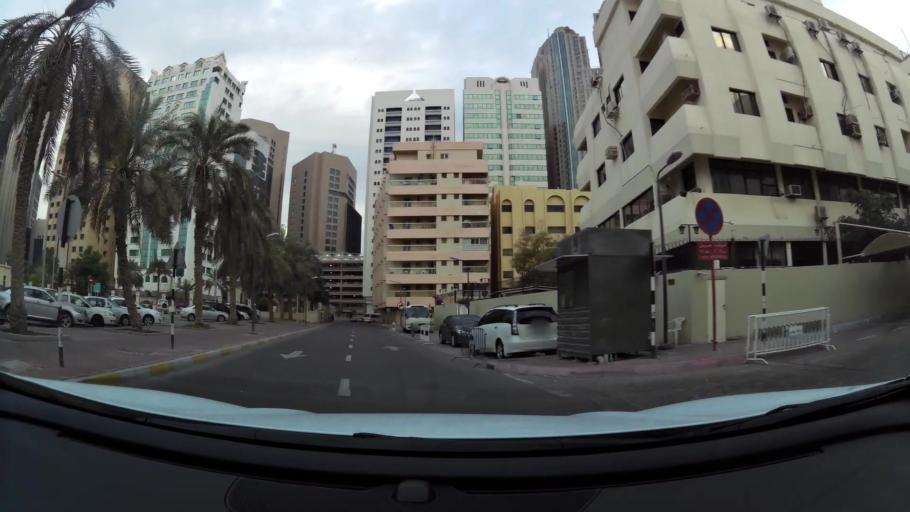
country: AE
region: Abu Dhabi
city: Abu Dhabi
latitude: 24.4964
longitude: 54.3684
